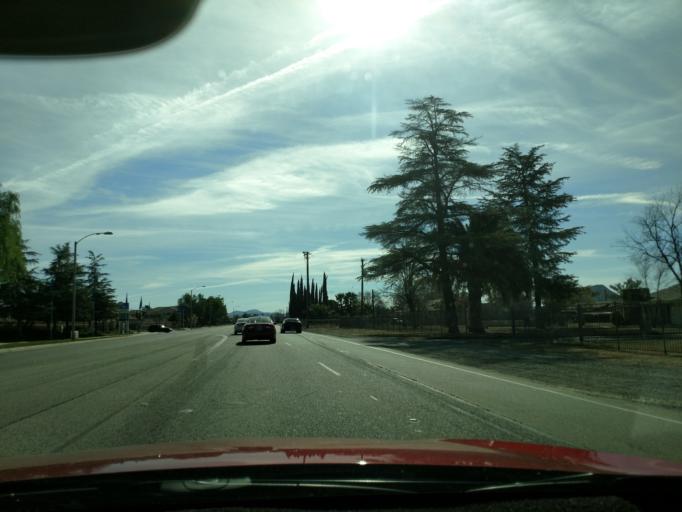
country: US
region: California
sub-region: Riverside County
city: San Jacinto
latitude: 33.7846
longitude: -117.0068
